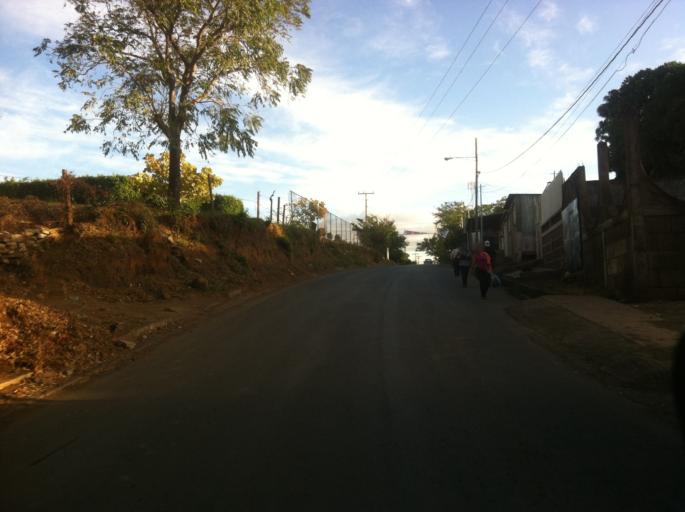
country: NI
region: Managua
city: Managua
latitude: 12.1040
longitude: -86.3086
